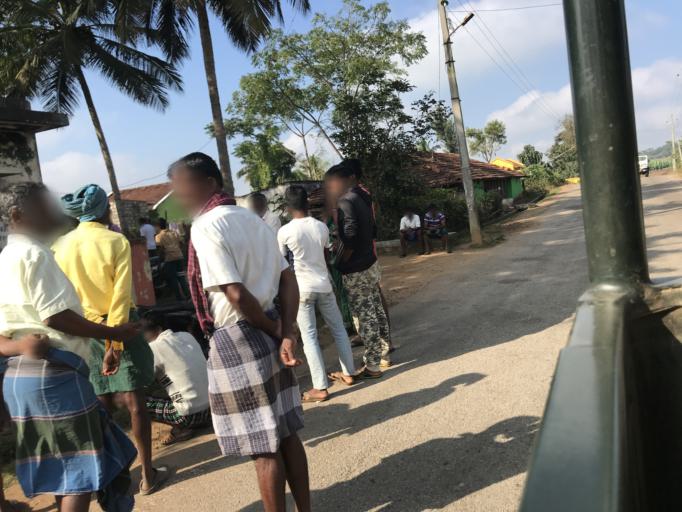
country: IN
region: Karnataka
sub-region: Mysore
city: Heggadadevankote
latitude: 11.9434
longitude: 76.2456
